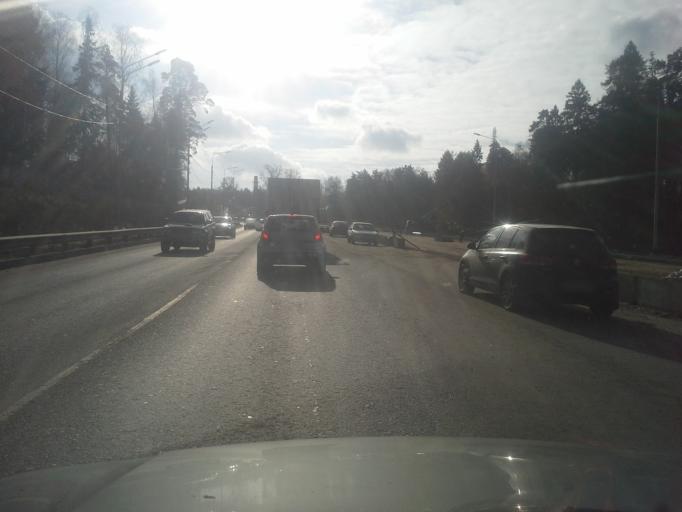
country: RU
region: Moskovskaya
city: Zvenigorod
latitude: 55.7098
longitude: 36.8741
